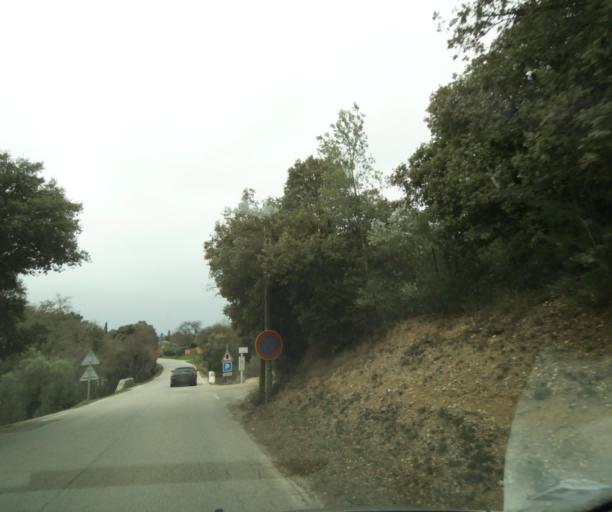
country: FR
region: Provence-Alpes-Cote d'Azur
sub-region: Departement des Bouches-du-Rhone
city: Chateauneuf-le-Rouge
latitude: 43.5537
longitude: 5.5807
